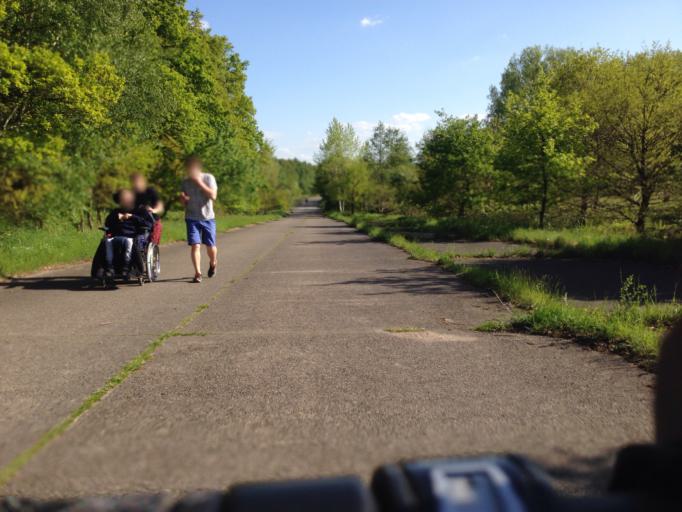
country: DE
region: Schleswig-Holstein
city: Stapelfeld
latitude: 53.6254
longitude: 10.2079
